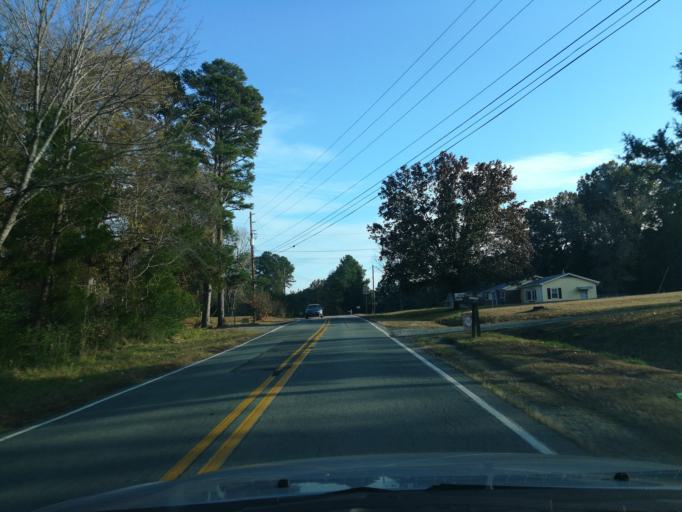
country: US
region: North Carolina
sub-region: Orange County
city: Chapel Hill
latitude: 35.9623
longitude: -79.0002
